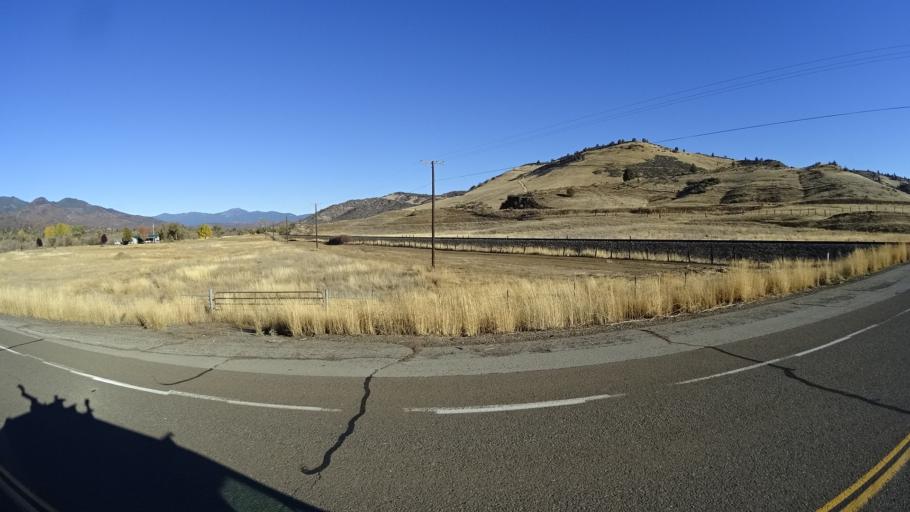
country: US
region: California
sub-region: Siskiyou County
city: Montague
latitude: 41.8977
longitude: -122.5445
